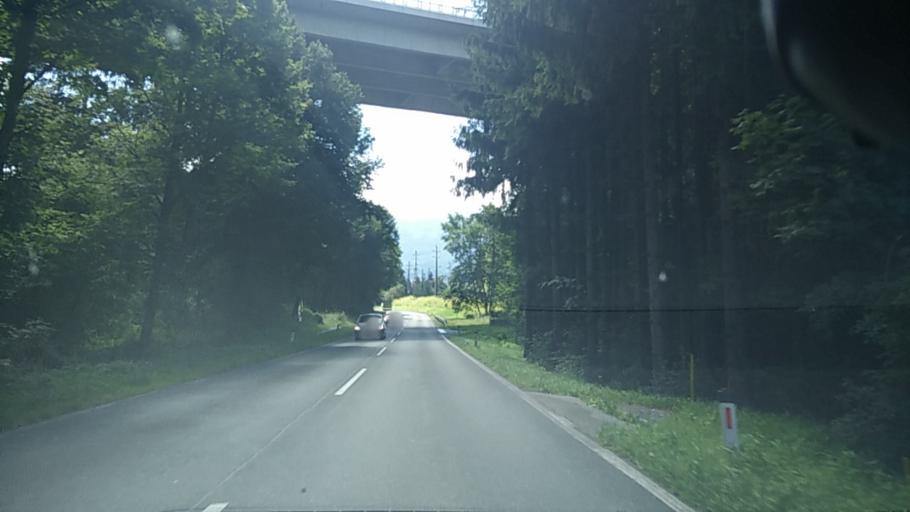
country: AT
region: Carinthia
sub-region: Politischer Bezirk Villach Land
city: Finkenstein am Faaker See
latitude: 46.5760
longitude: 13.8366
